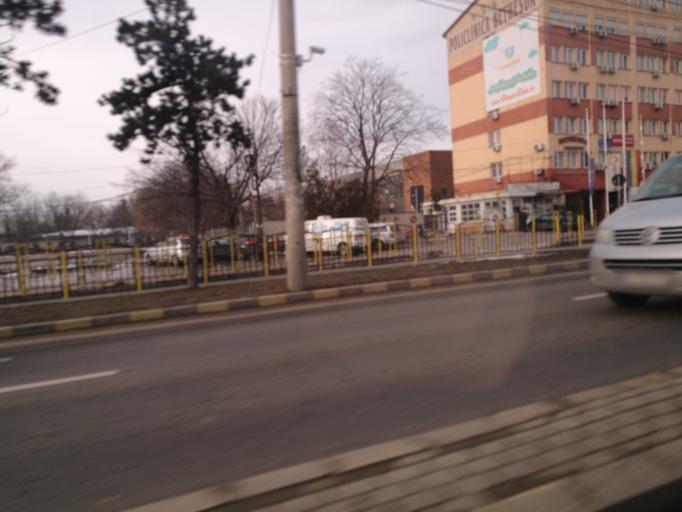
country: RO
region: Suceava
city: Suceava
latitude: 47.6608
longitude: 26.2659
